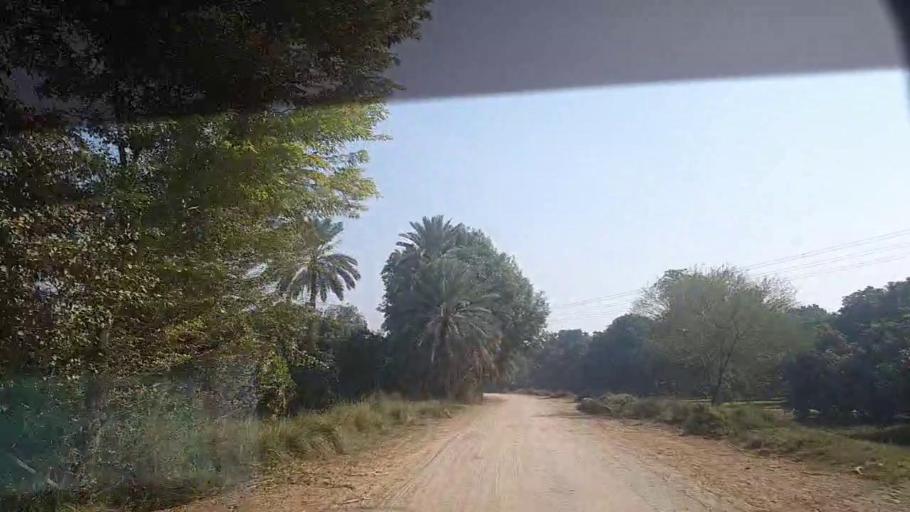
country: PK
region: Sindh
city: Khairpur
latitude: 27.4574
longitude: 68.7436
